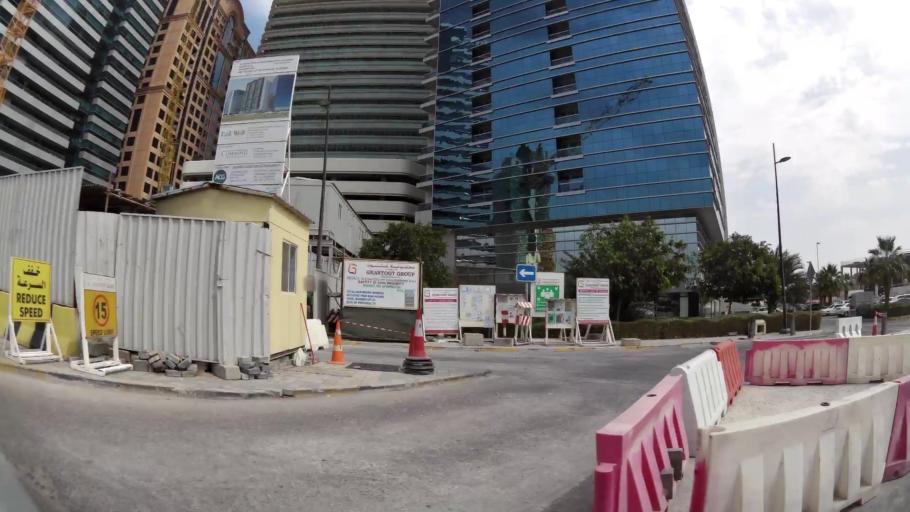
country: AE
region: Abu Dhabi
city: Abu Dhabi
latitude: 24.4677
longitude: 54.3391
